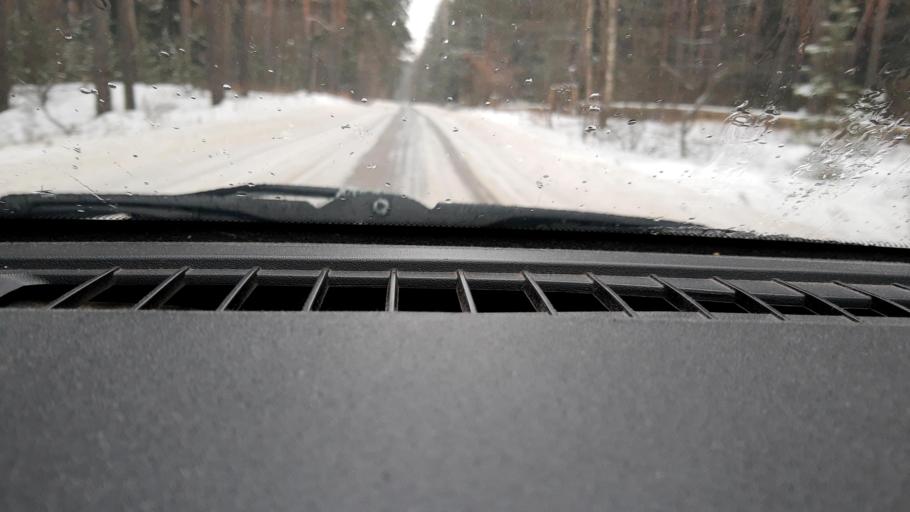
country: RU
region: Nizjnij Novgorod
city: Afonino
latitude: 56.1850
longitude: 44.0796
